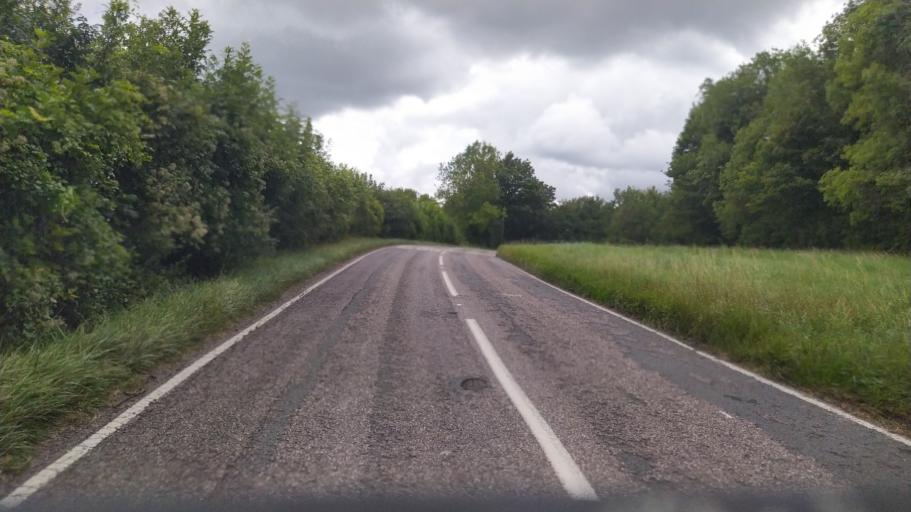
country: GB
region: England
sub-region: Wiltshire
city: Bower Chalke
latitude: 50.9237
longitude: -1.9468
